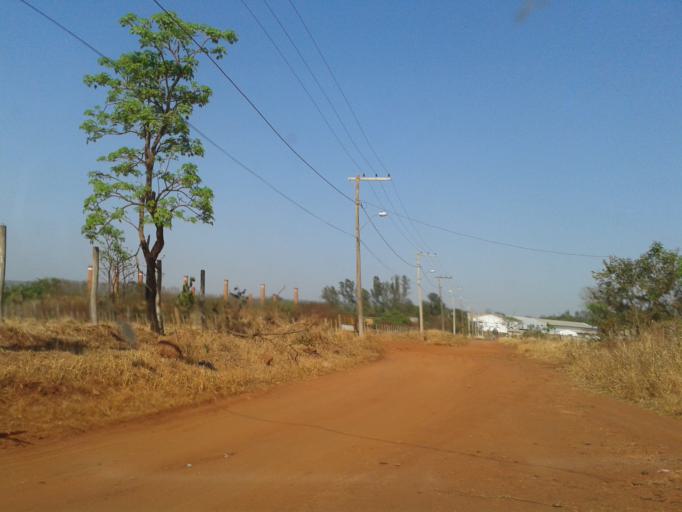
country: BR
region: Minas Gerais
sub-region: Ituiutaba
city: Ituiutaba
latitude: -18.9607
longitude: -49.4875
